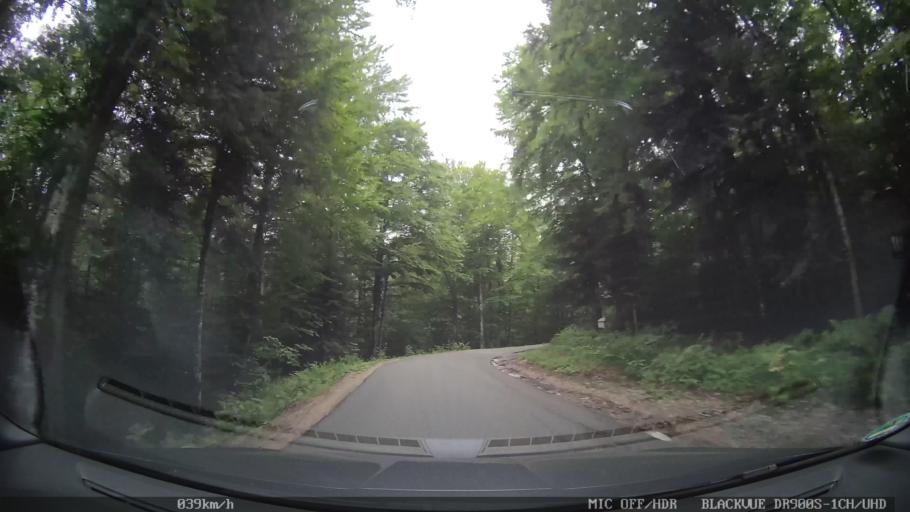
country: HR
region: Licko-Senjska
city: Jezerce
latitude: 44.9264
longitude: 15.5733
